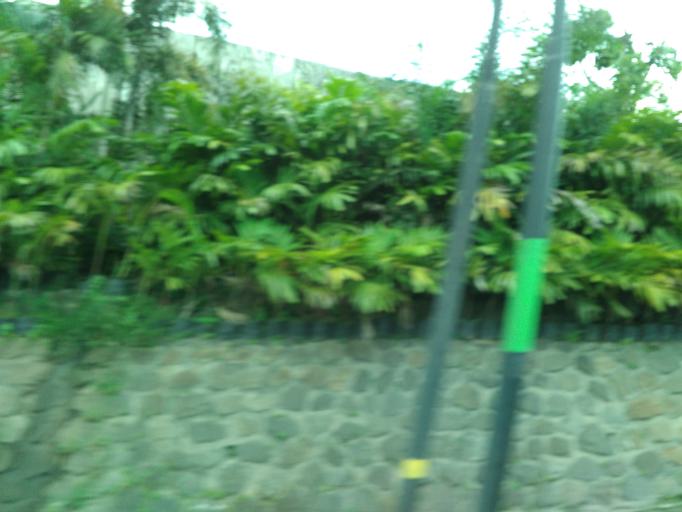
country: ID
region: Central Java
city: Ceper
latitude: -7.6572
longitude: 110.6779
